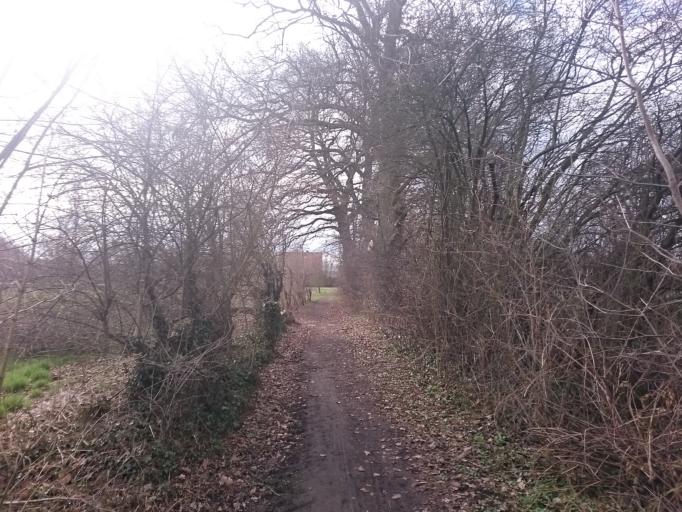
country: DE
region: Lower Saxony
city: Lauenhagen
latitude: 52.3572
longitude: 9.2026
